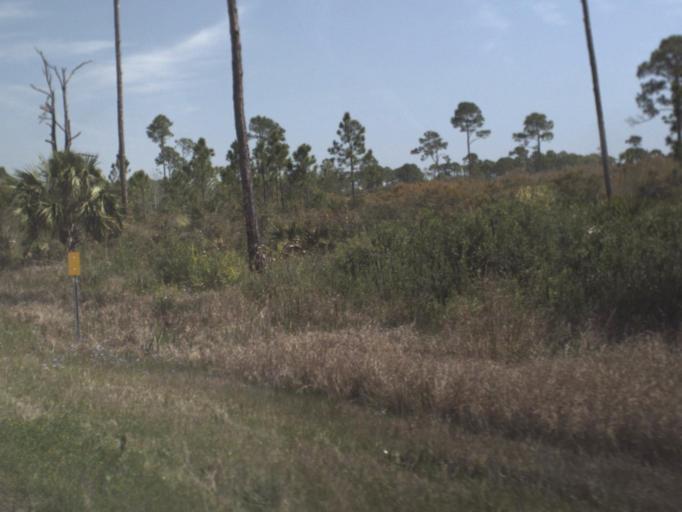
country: US
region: Florida
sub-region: Gulf County
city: Port Saint Joe
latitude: 29.6812
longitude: -85.3380
